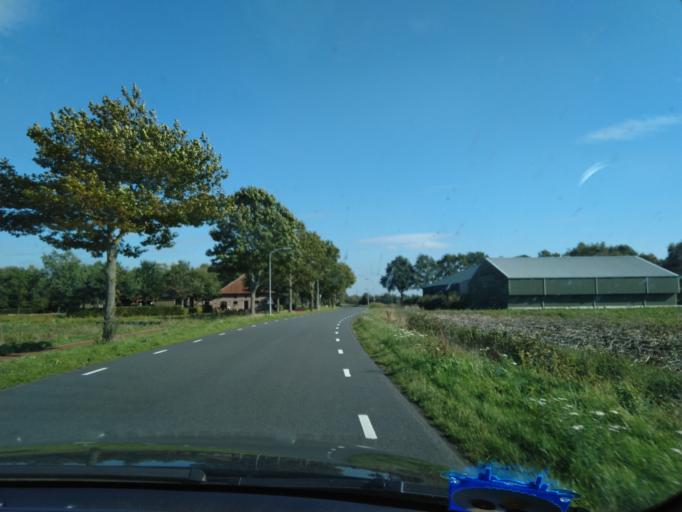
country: NL
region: Groningen
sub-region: Gemeente Veendam
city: Veendam
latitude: 53.0913
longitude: 6.8319
